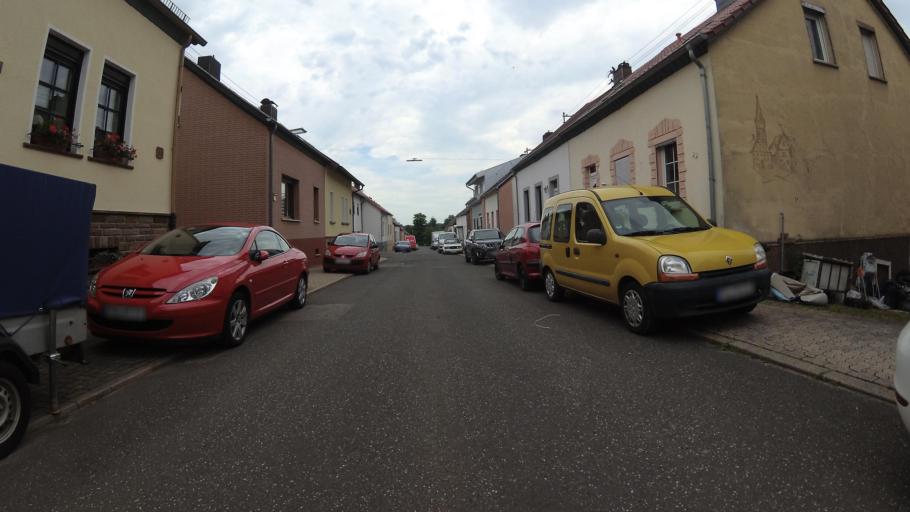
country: DE
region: Saarland
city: Friedrichsthal
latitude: 49.3325
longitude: 7.0853
